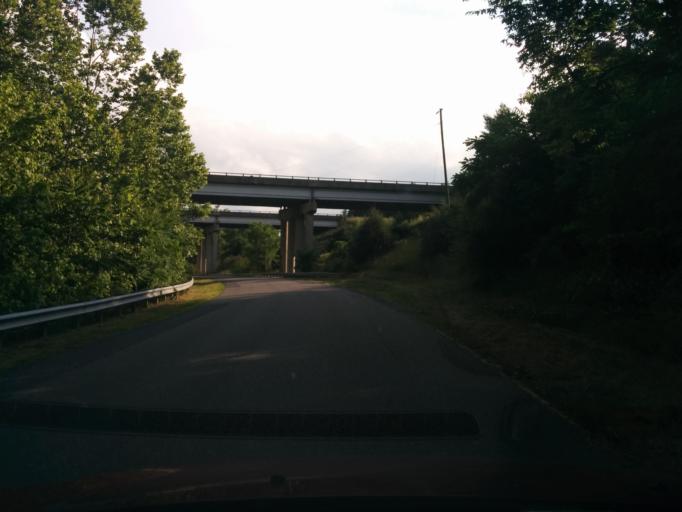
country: US
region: Virginia
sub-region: Rockbridge County
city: East Lexington
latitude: 37.7991
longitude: -79.4083
